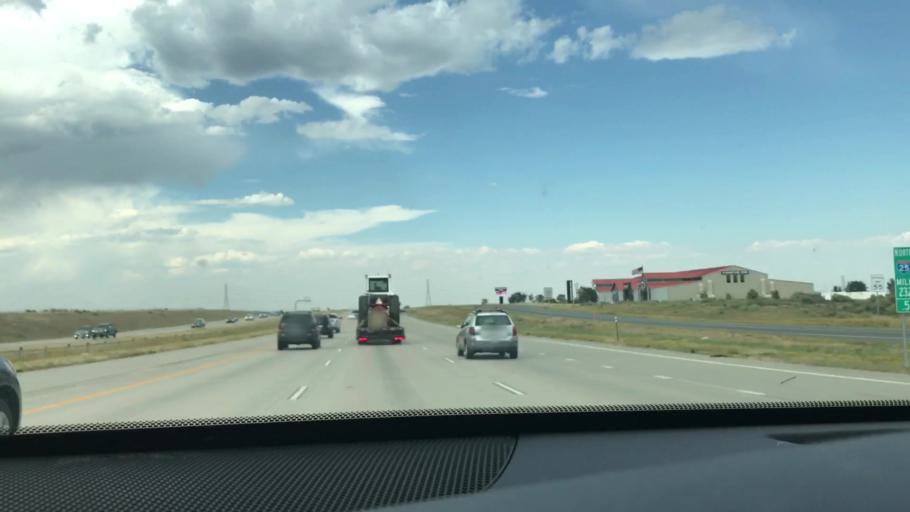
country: US
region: Colorado
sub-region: Weld County
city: Dacono
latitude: 40.0496
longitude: -104.9794
